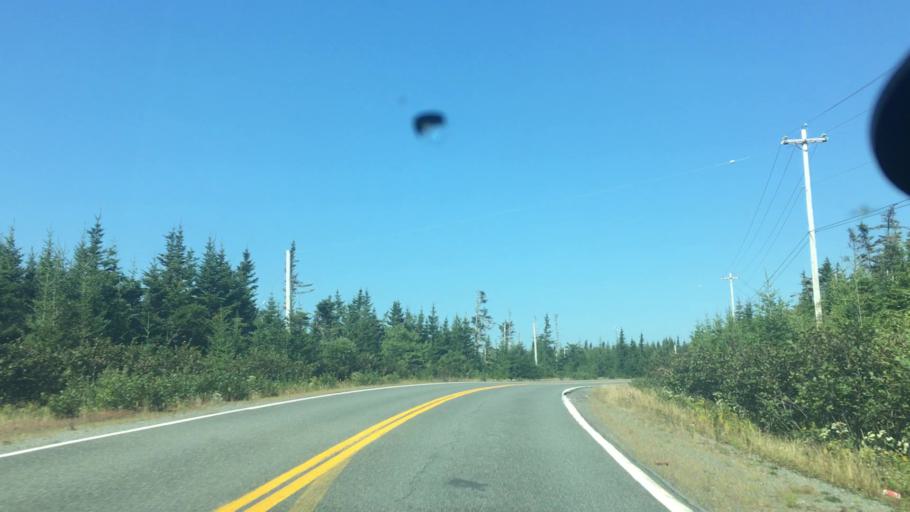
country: CA
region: Nova Scotia
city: Antigonish
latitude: 44.9839
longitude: -62.0957
